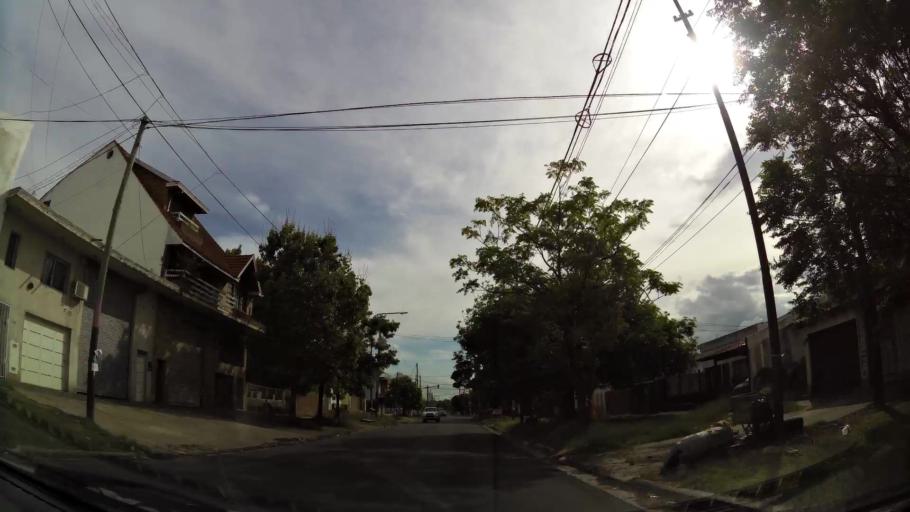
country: AR
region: Buenos Aires
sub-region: Partido de Quilmes
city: Quilmes
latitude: -34.7453
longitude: -58.2762
